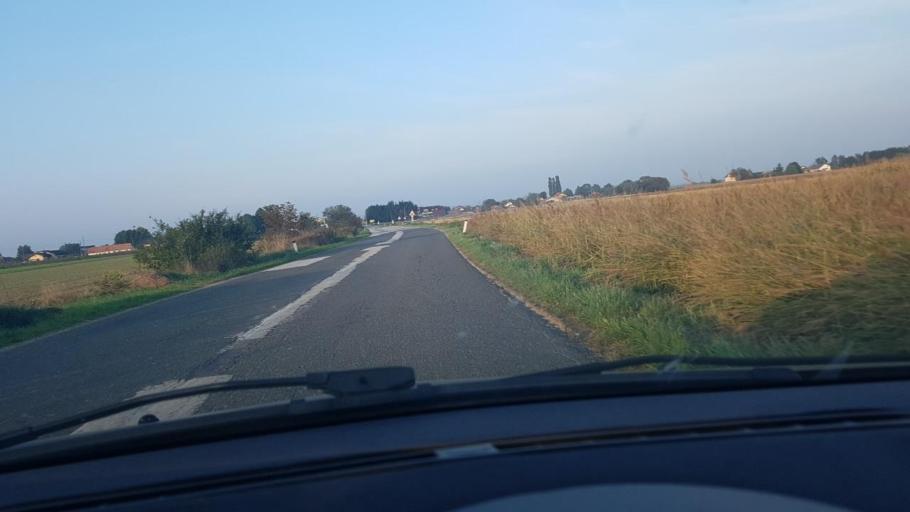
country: SI
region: Slovenska Bistrica
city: Pragersko
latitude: 46.3982
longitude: 15.6946
